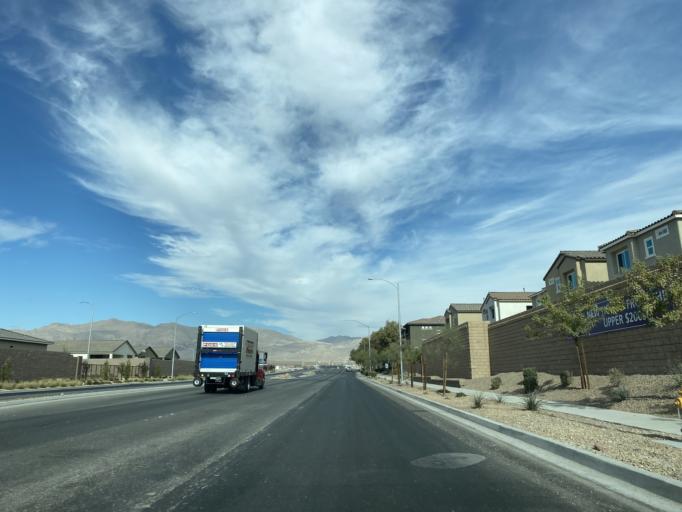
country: US
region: Nevada
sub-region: Clark County
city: Nellis Air Force Base
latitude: 36.2809
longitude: -115.1168
